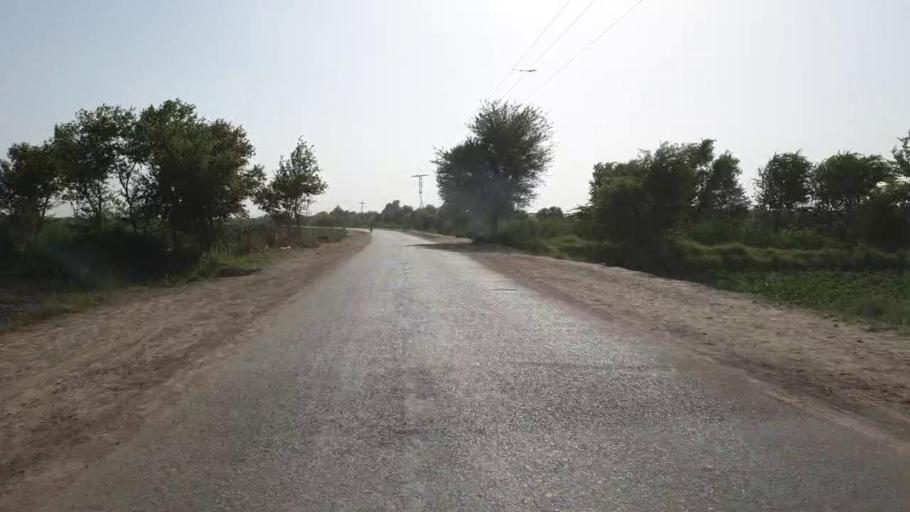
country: PK
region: Sindh
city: Daur
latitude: 26.4759
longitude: 68.4649
